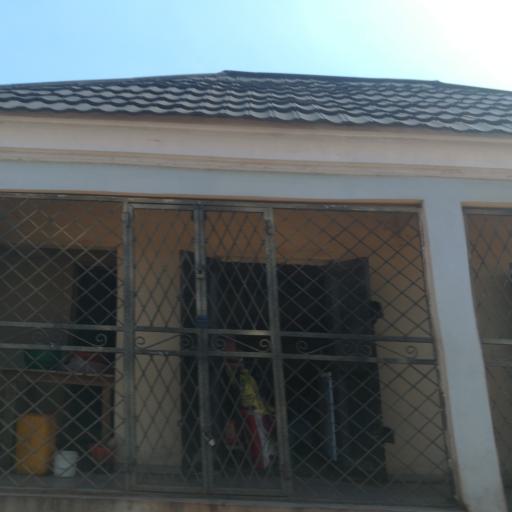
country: NG
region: Plateau
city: Bukuru
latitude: 9.8421
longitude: 8.9050
